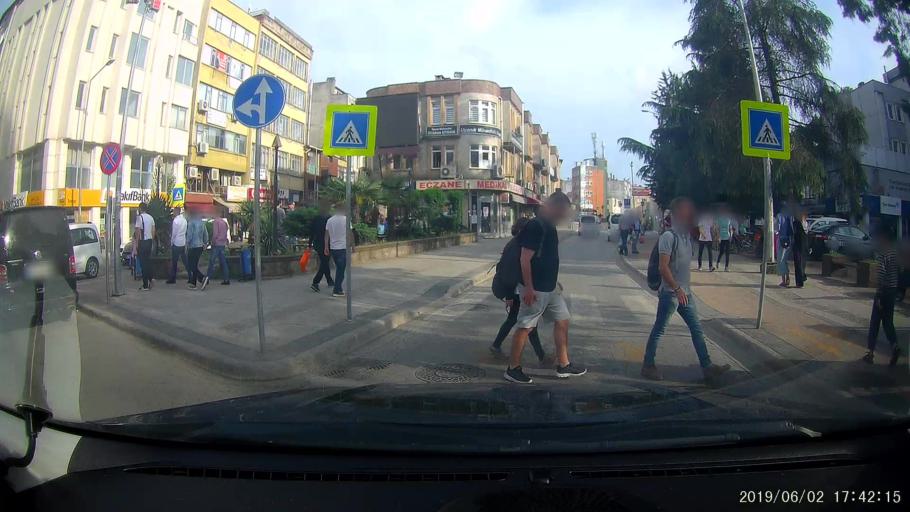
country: TR
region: Samsun
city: Terme
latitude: 41.2092
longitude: 36.9720
